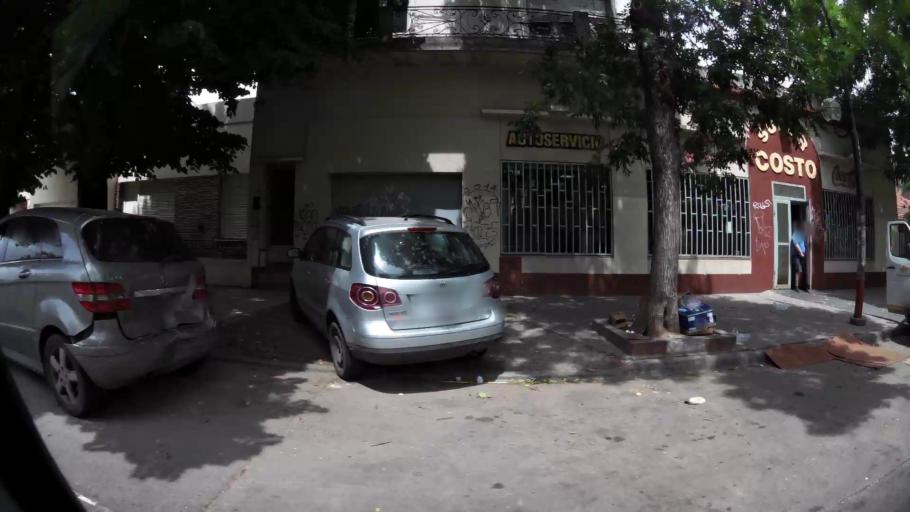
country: AR
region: Buenos Aires
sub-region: Partido de La Plata
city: La Plata
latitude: -34.9394
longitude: -57.9494
